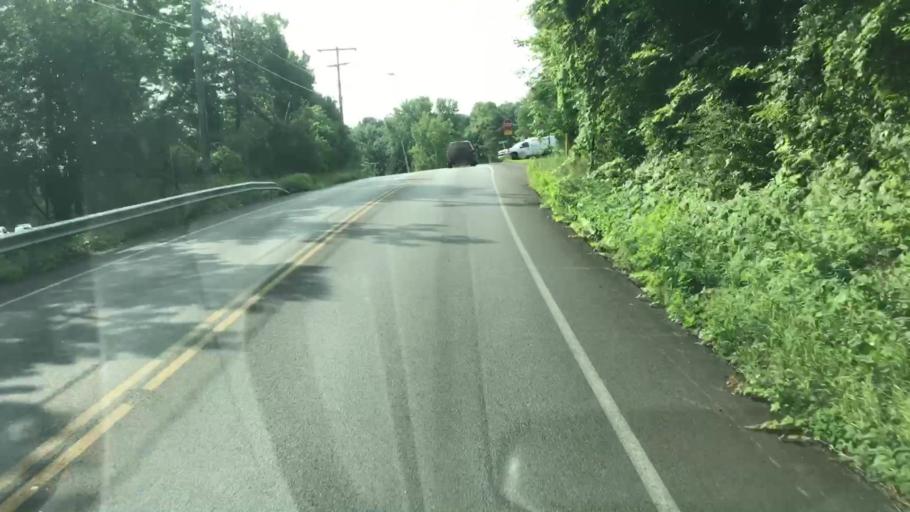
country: US
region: New York
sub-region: Onondaga County
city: Fayetteville
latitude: 43.0100
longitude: -76.0116
